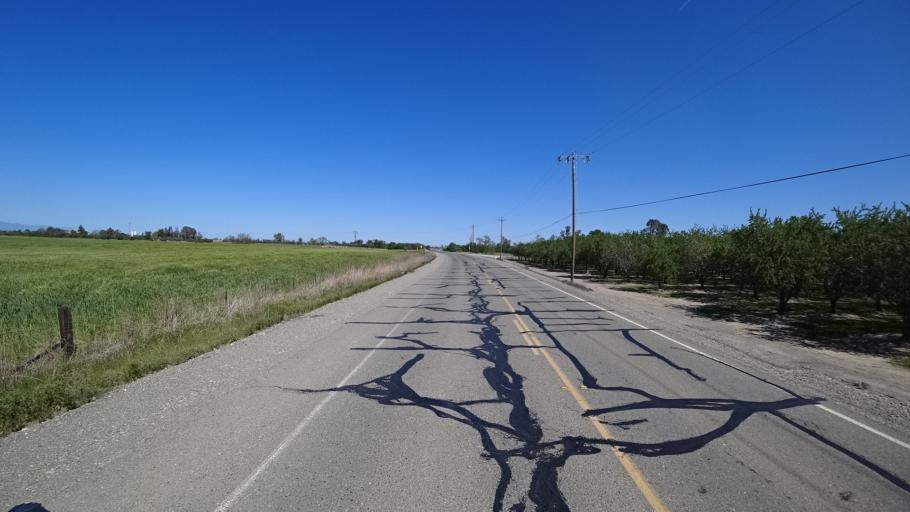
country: US
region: California
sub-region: Glenn County
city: Hamilton City
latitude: 39.7412
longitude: -122.1043
